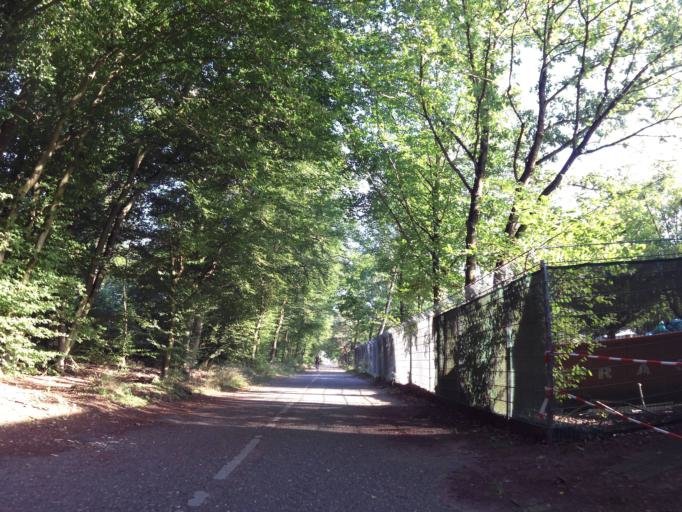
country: DE
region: Hesse
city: Morfelden-Walldorf
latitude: 50.0201
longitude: 8.6233
